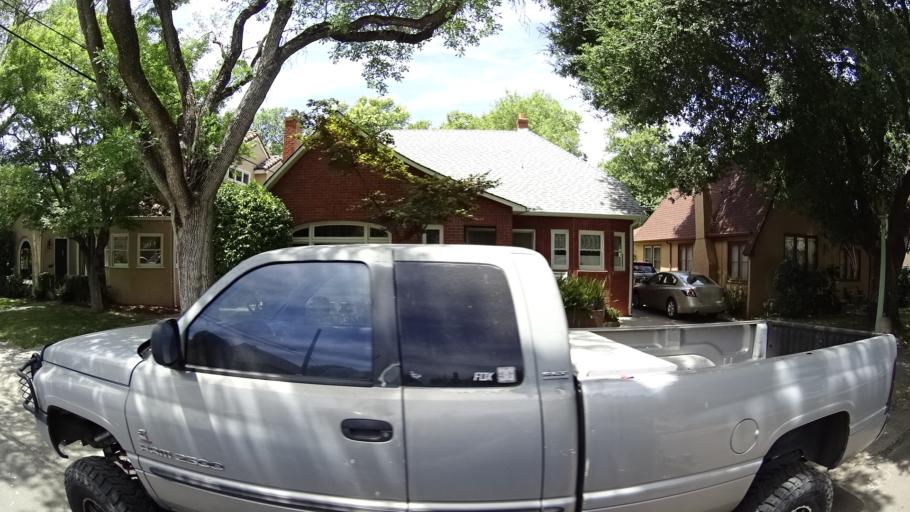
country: US
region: California
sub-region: Sacramento County
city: Sacramento
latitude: 38.5621
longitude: -121.4535
